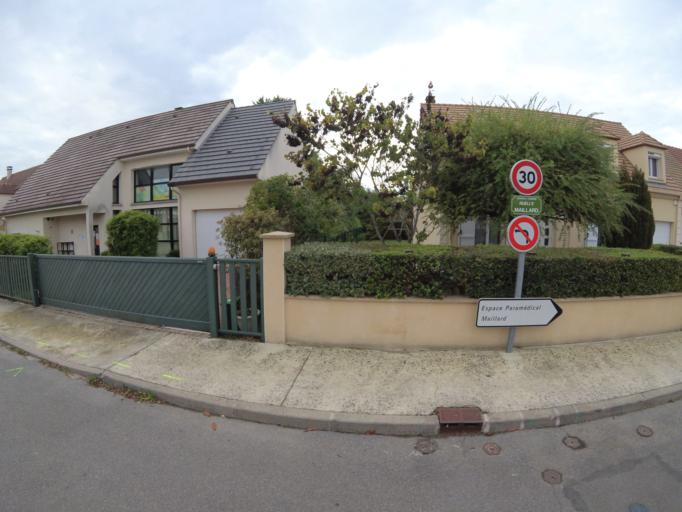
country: FR
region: Ile-de-France
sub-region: Departement de Seine-et-Marne
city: Lagny-sur-Marne
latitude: 48.8642
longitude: 2.7152
